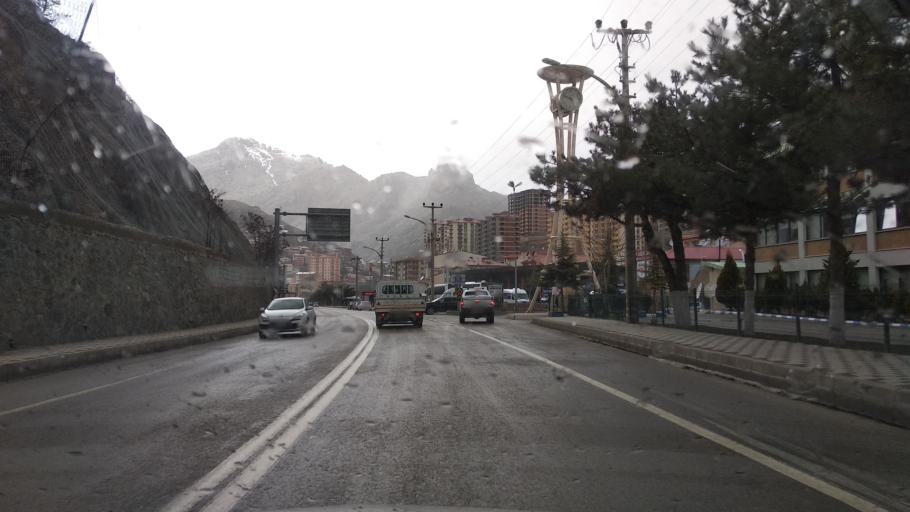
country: TR
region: Gumushane
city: Gumushkhane
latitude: 40.4600
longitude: 39.4737
